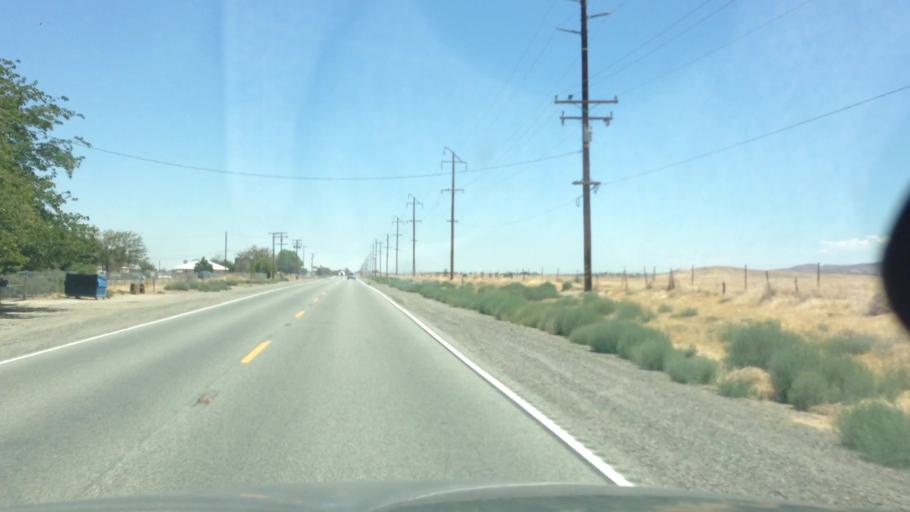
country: US
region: California
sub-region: Kern County
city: Lebec
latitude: 34.7833
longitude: -118.6317
